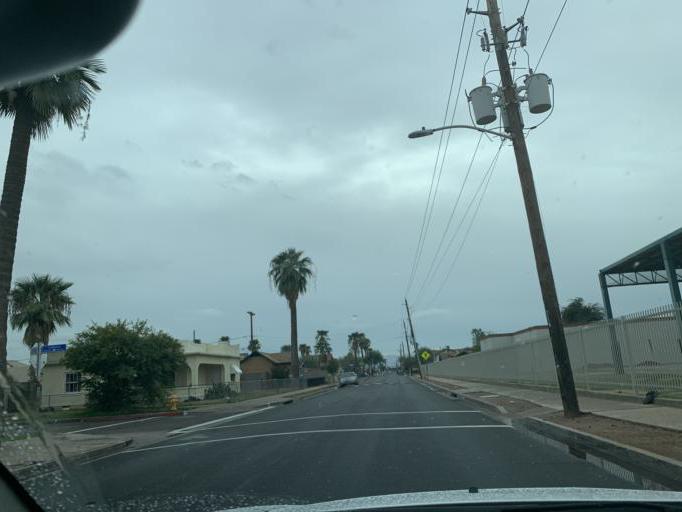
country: US
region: Arizona
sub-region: Maricopa County
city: Phoenix
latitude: 33.4579
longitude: -112.0521
